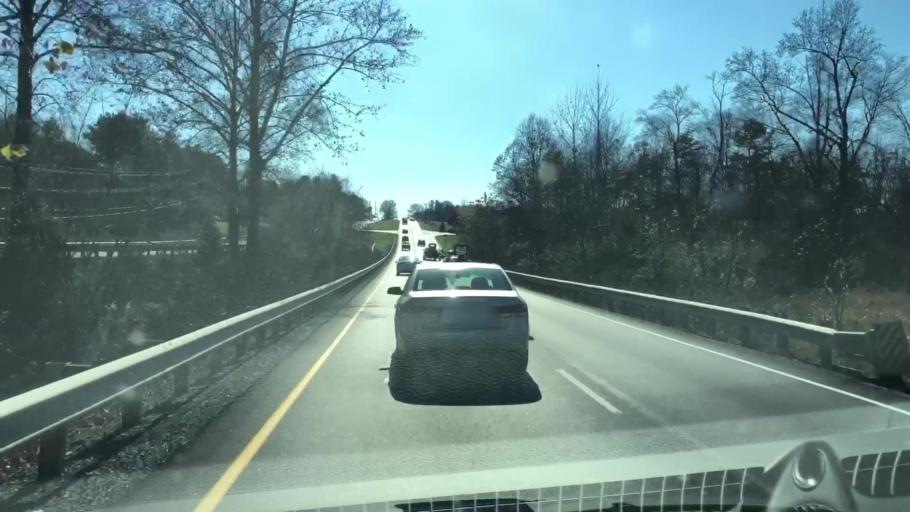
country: US
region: Virginia
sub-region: Greene County
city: Ruckersville
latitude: 38.2156
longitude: -78.3811
